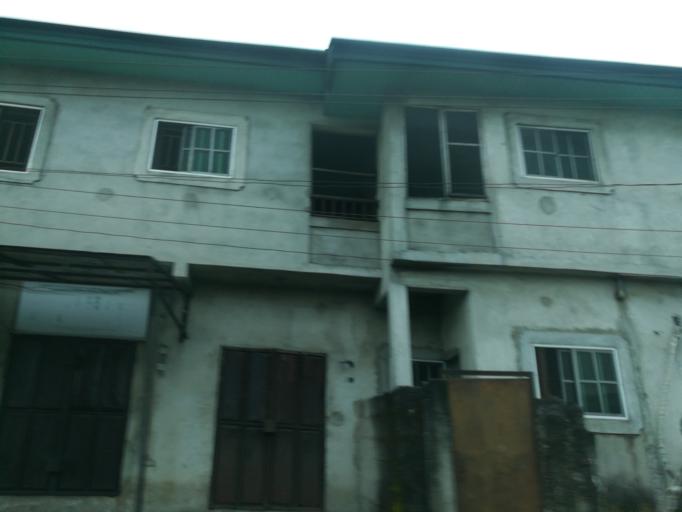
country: NG
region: Rivers
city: Port Harcourt
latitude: 4.8265
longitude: 7.0212
